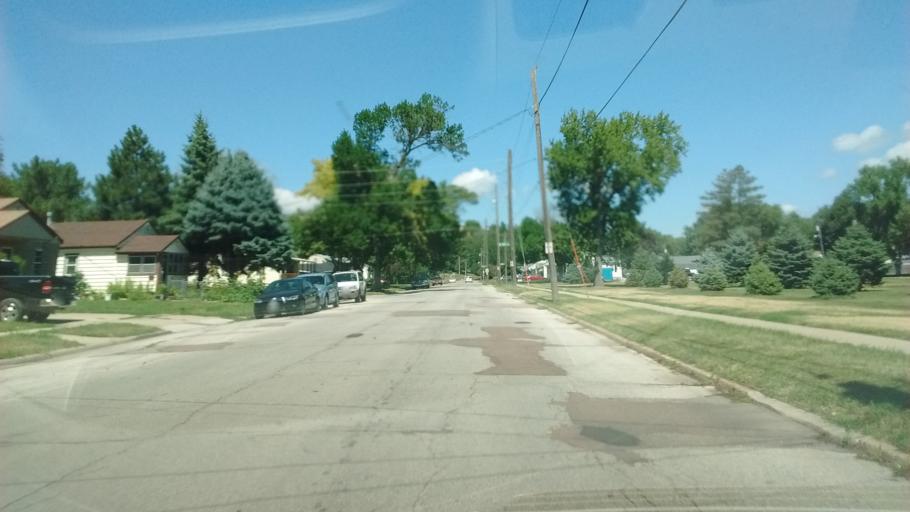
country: US
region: Iowa
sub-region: Woodbury County
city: Sioux City
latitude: 42.5211
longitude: -96.4256
